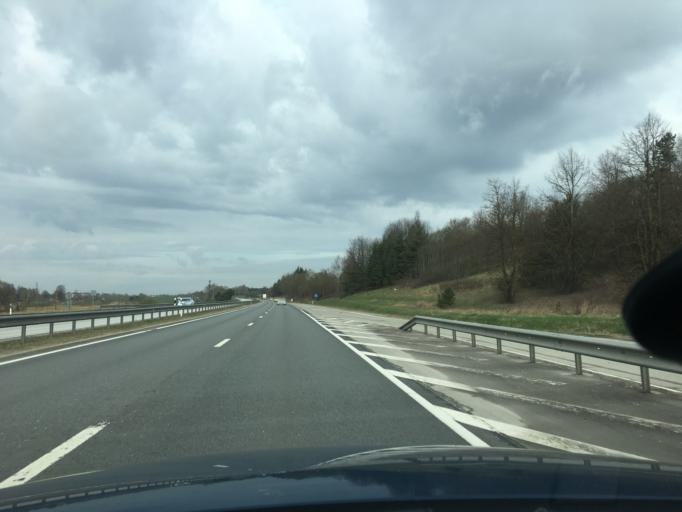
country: LV
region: Ikskile
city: Ikskile
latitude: 56.8449
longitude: 24.4734
